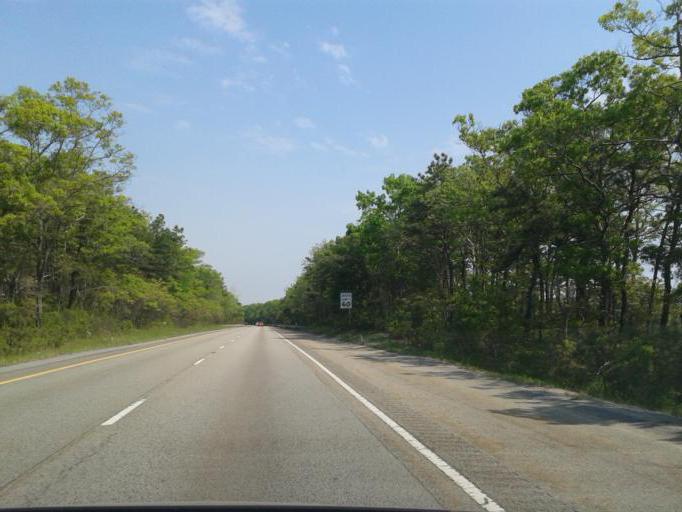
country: US
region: Massachusetts
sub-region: Barnstable County
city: Sagamore
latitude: 41.7938
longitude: -70.5447
